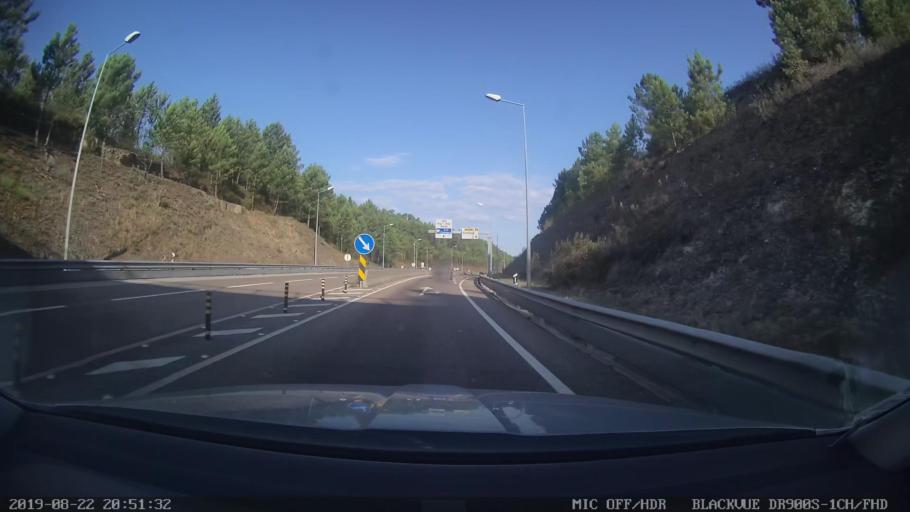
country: PT
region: Castelo Branco
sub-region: Proenca-A-Nova
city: Proenca-a-Nova
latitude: 39.7602
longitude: -7.9615
